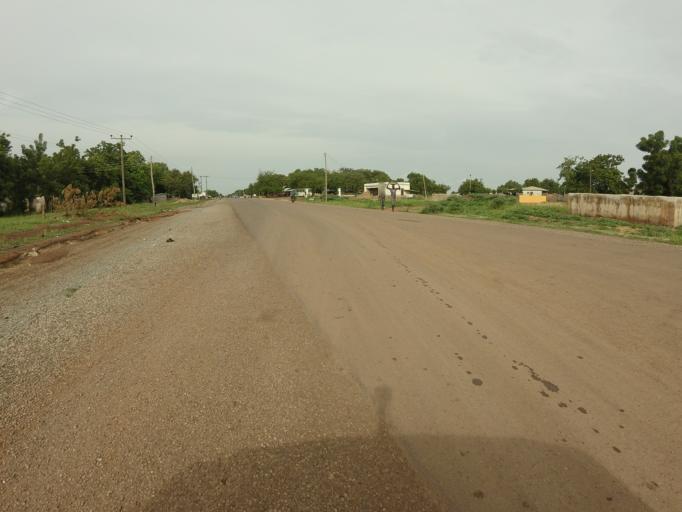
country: GH
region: Northern
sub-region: Yendi
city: Yendi
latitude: 9.9264
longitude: -0.2113
